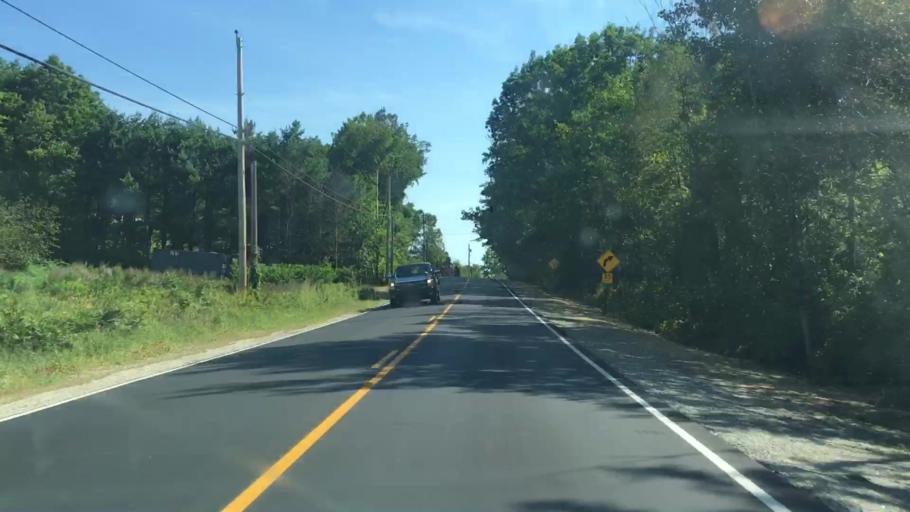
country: US
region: Maine
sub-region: Androscoggin County
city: Sabattus
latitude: 44.1252
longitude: -70.0858
